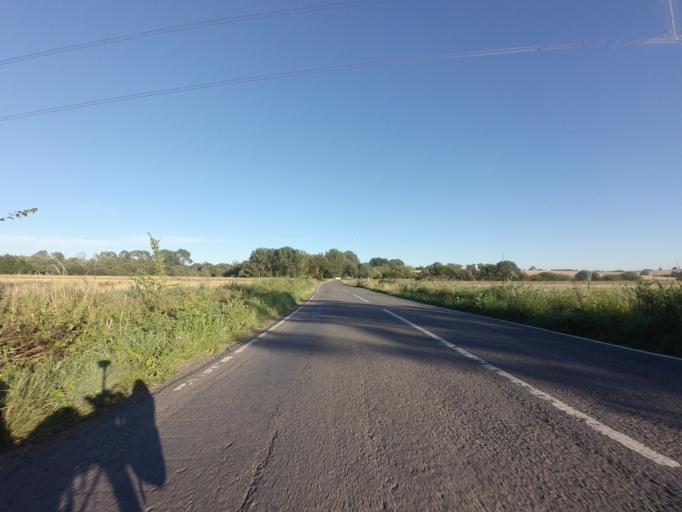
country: GB
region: England
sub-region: Kent
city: Sturry
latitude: 51.3295
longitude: 1.1909
